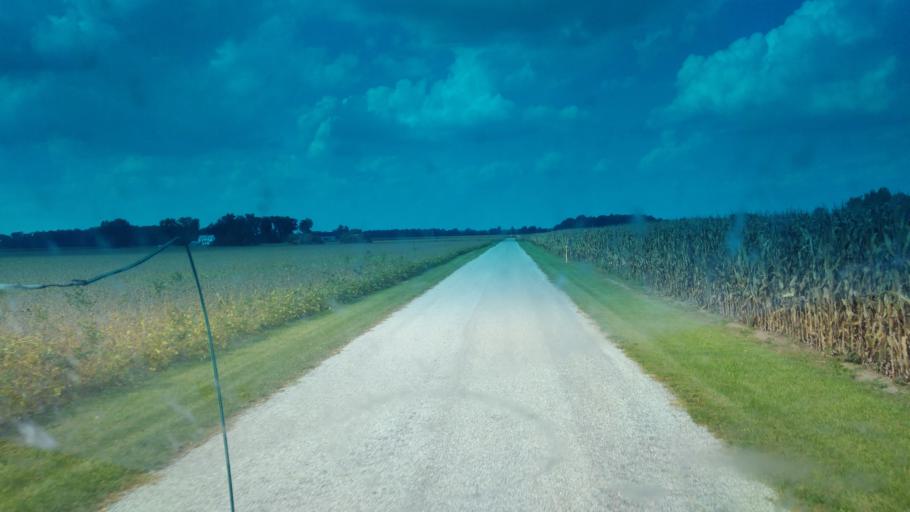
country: US
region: Ohio
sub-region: Hardin County
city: Kenton
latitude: 40.7267
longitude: -83.6144
